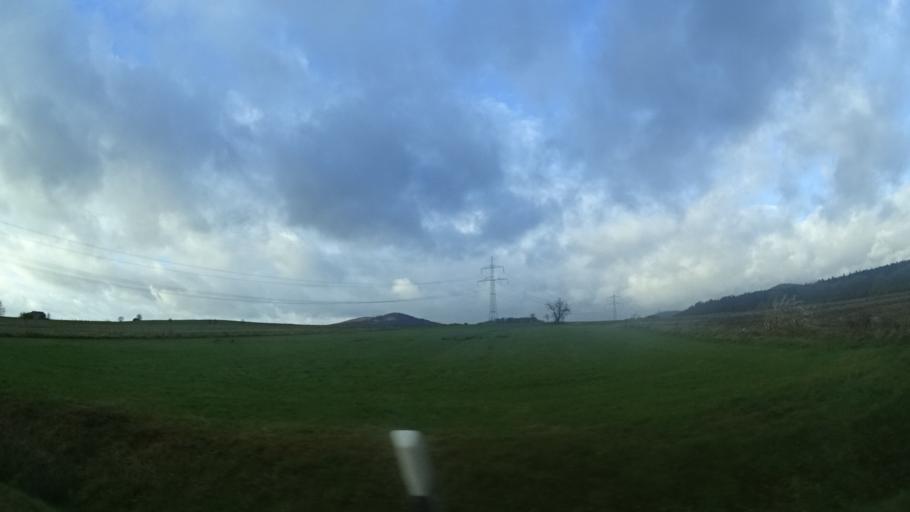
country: DE
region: Hesse
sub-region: Regierungsbezirk Kassel
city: Hunfeld
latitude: 50.7018
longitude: 9.8257
